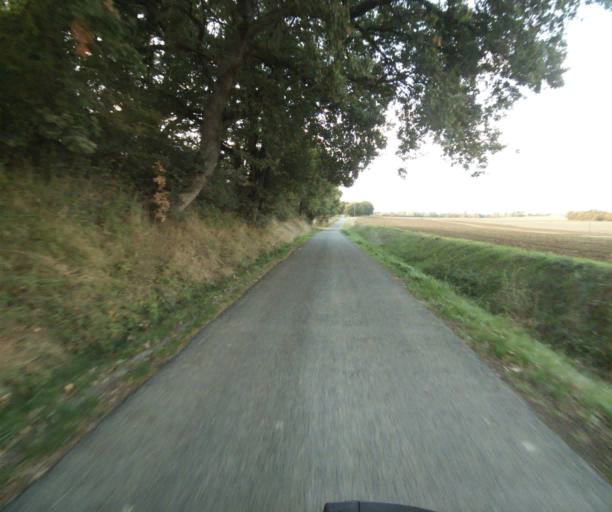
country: FR
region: Midi-Pyrenees
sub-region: Departement du Tarn-et-Garonne
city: Verdun-sur-Garonne
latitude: 43.8294
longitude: 1.2065
